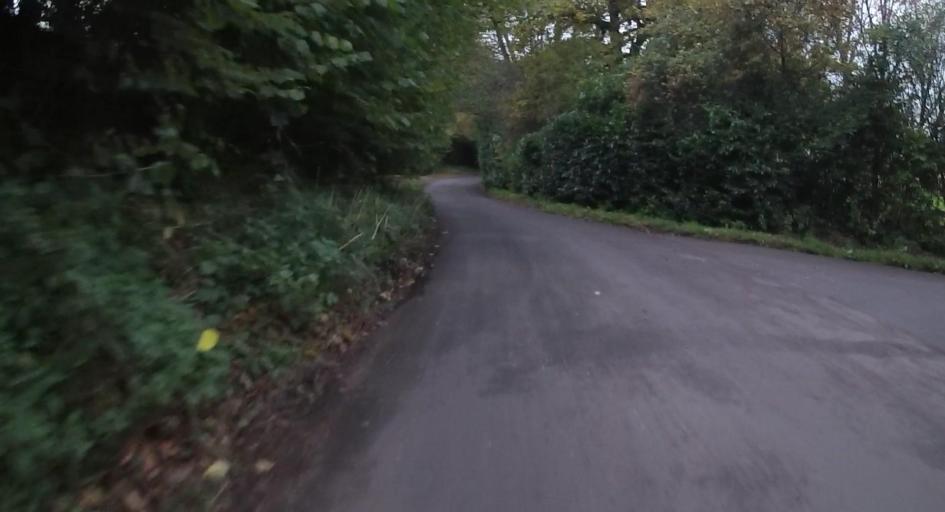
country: GB
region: England
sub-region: Hampshire
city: Lindford
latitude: 51.1273
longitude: -0.8297
